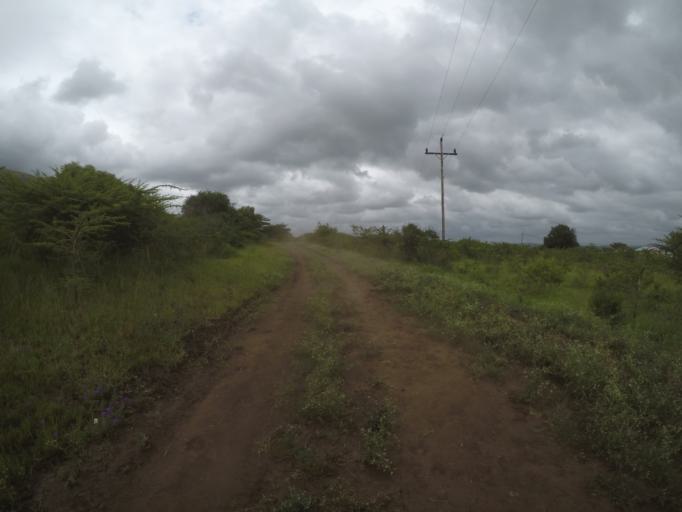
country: ZA
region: KwaZulu-Natal
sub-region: uThungulu District Municipality
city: Empangeni
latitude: -28.5624
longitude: 31.8777
